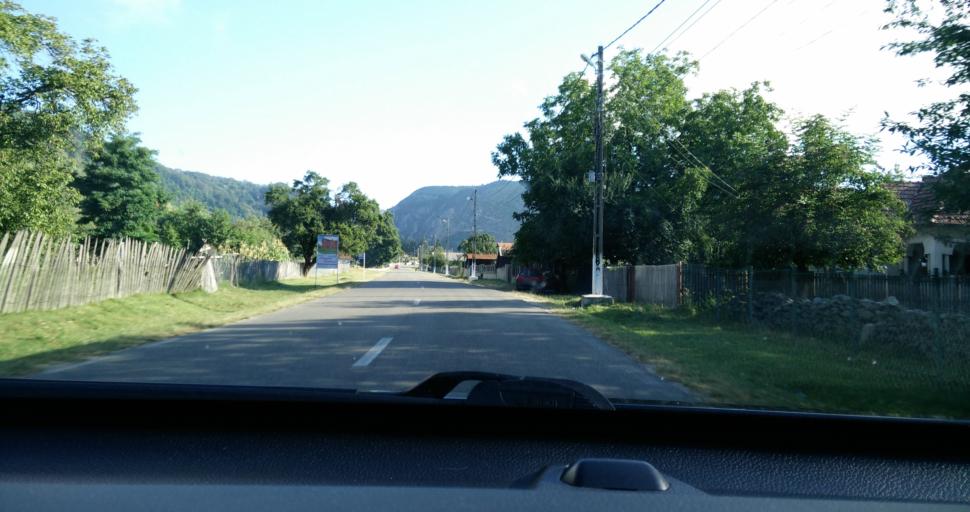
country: RO
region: Gorj
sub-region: Comuna Baia de Fier
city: Baia de Fier
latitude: 45.1730
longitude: 23.7551
